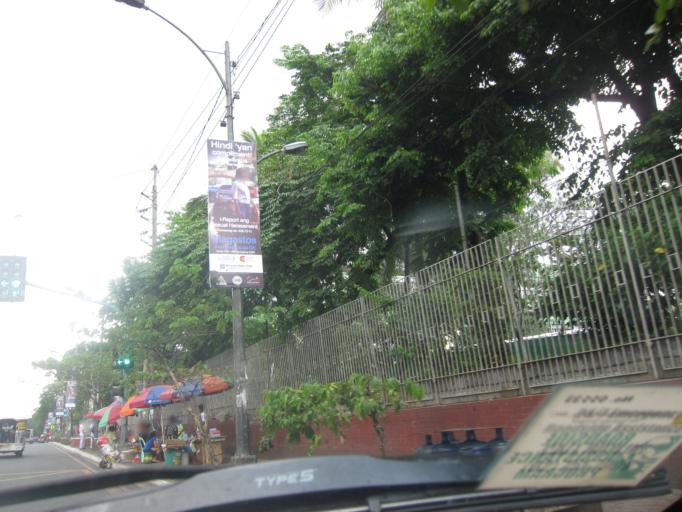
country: PH
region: Metro Manila
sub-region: Quezon City
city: Quezon City
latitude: 14.6410
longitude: 121.0470
